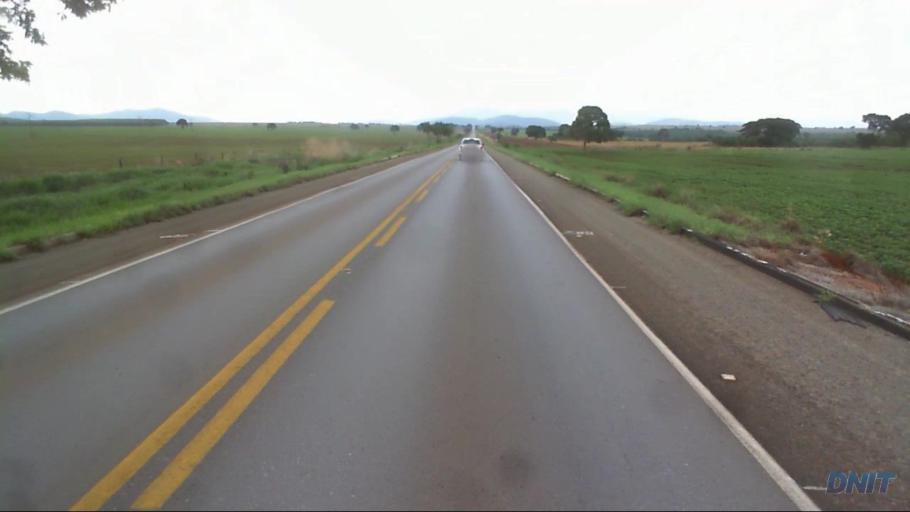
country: BR
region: Goias
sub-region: Barro Alto
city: Barro Alto
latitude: -14.8155
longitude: -49.0417
